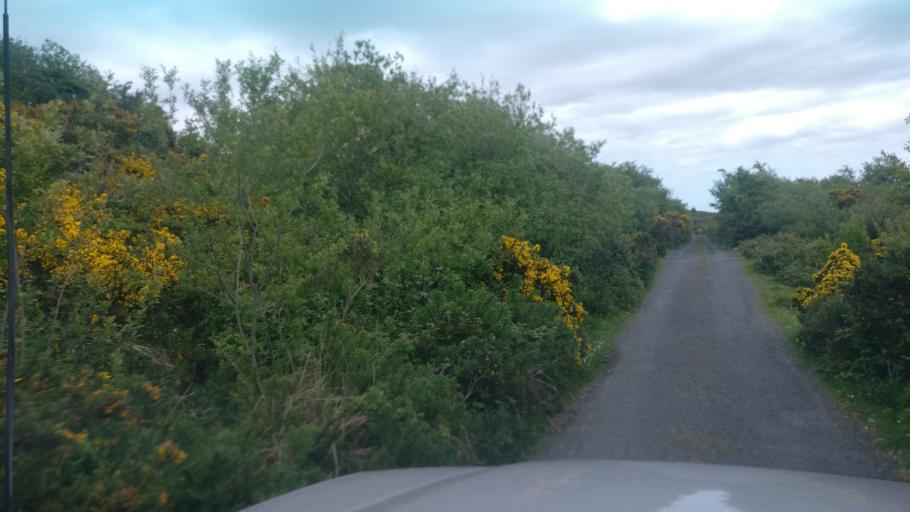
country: IE
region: Connaught
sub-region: County Galway
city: Loughrea
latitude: 53.1166
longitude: -8.6526
